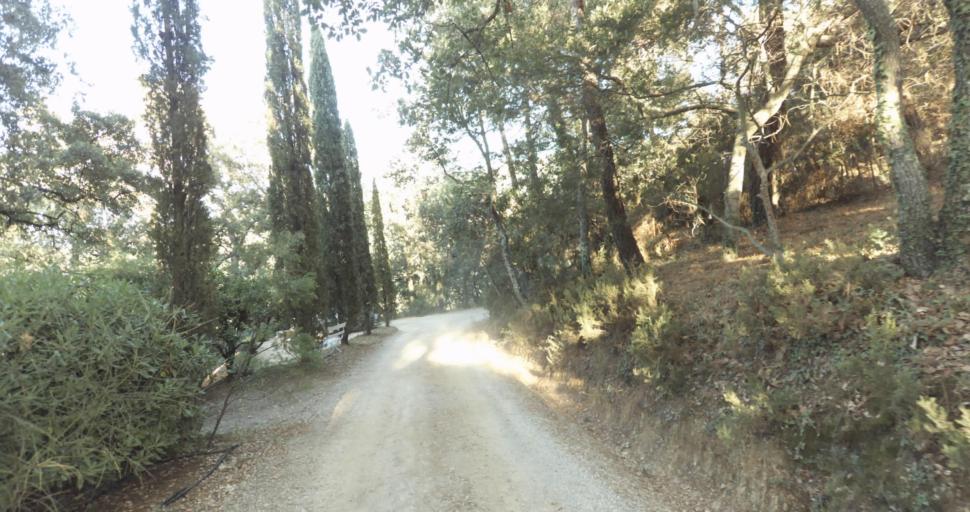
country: FR
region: Provence-Alpes-Cote d'Azur
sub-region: Departement du Var
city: Gassin
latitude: 43.2270
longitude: 6.5903
